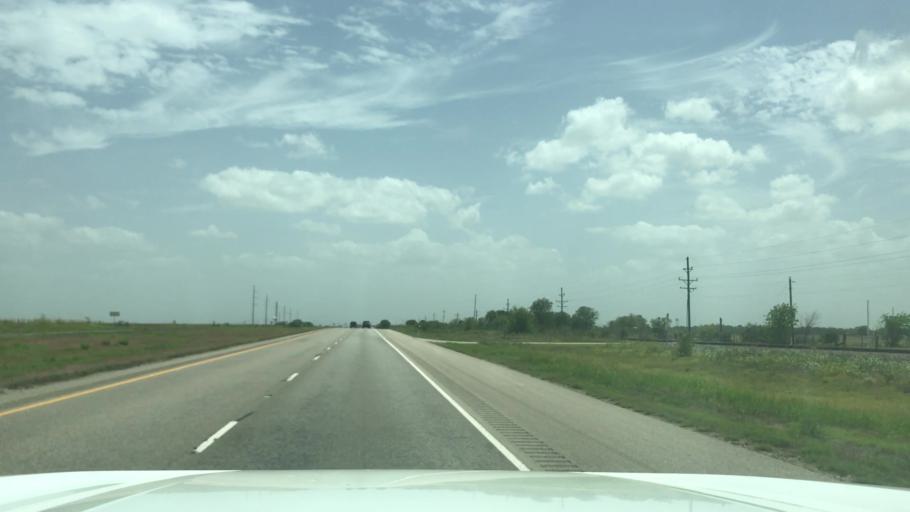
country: US
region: Texas
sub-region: Falls County
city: Marlin
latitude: 31.3425
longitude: -96.8935
